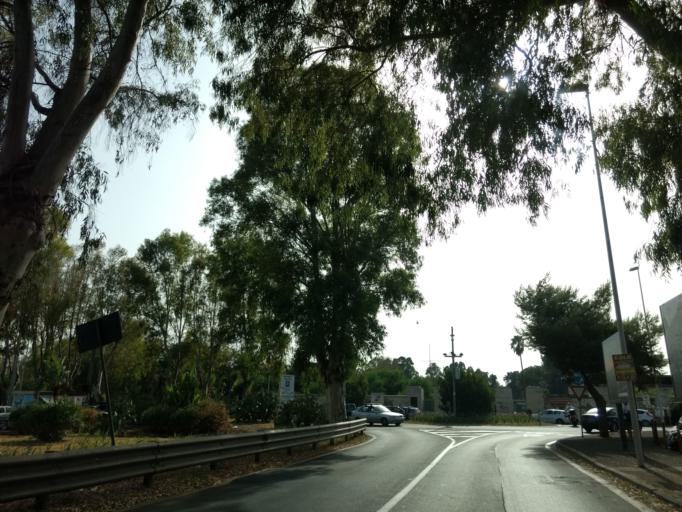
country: IT
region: Sicily
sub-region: Catania
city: Catania
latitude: 37.4739
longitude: 15.0666
